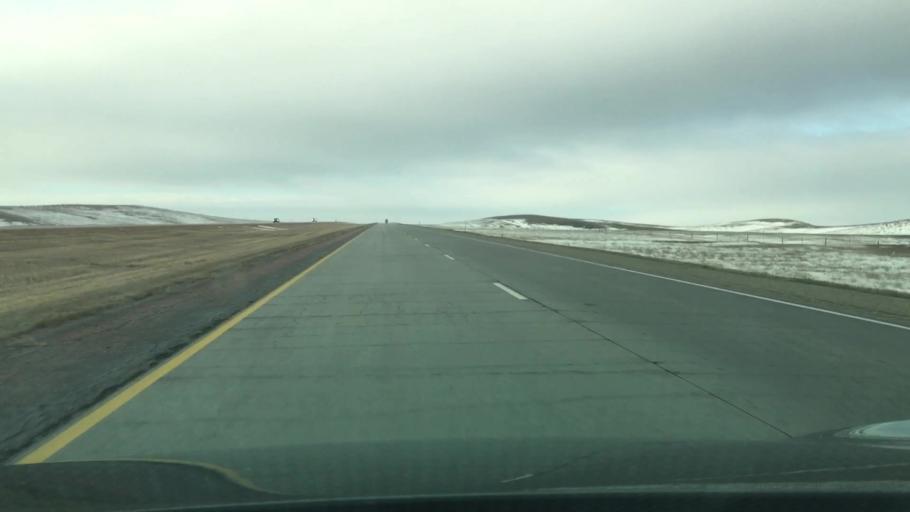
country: US
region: South Dakota
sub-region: Brule County
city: Chamberlain
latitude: 43.8300
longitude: -99.4612
